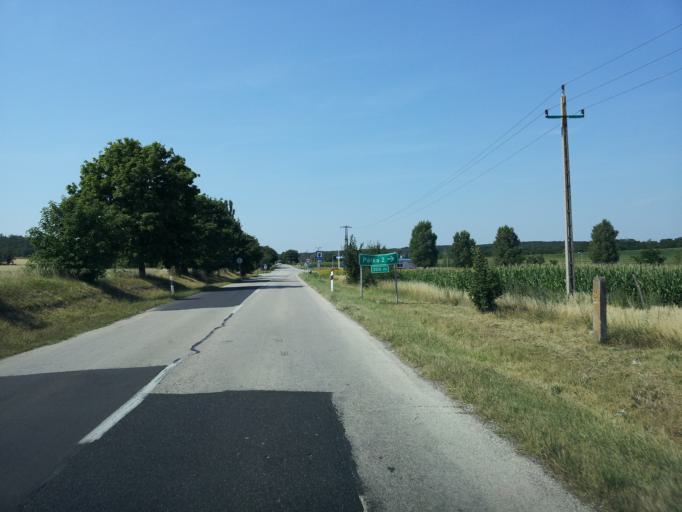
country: HU
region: Fejer
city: Pakozd
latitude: 47.2597
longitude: 18.5187
